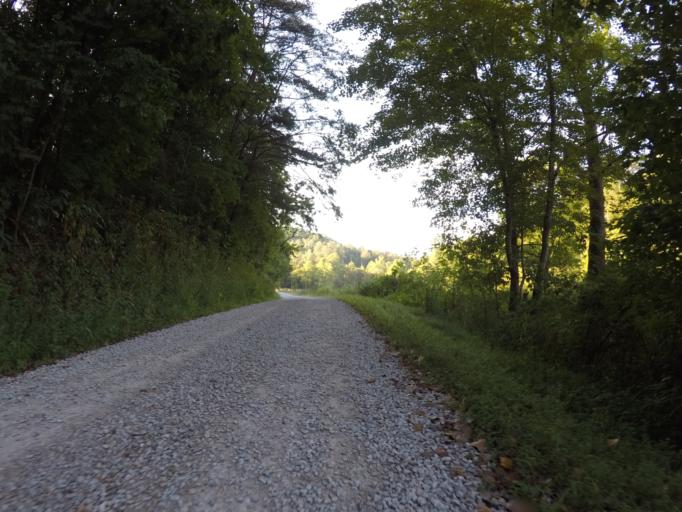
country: US
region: Ohio
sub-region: Lawrence County
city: Coal Grove
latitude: 38.5801
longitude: -82.5456
